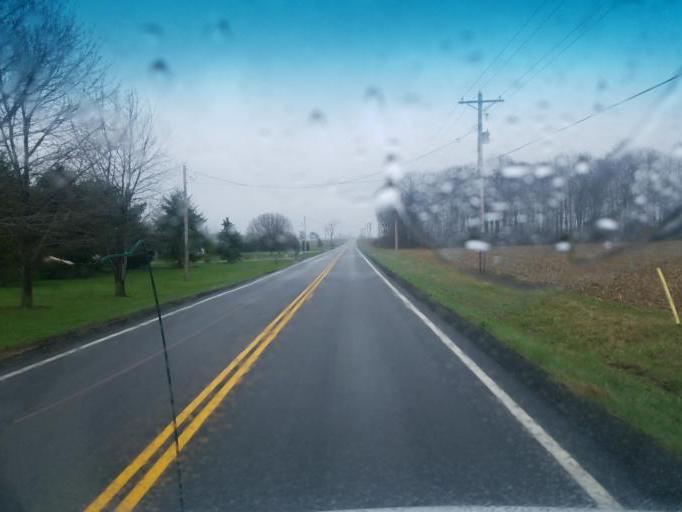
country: US
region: Ohio
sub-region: Crawford County
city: Bucyrus
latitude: 40.9649
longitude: -82.9235
